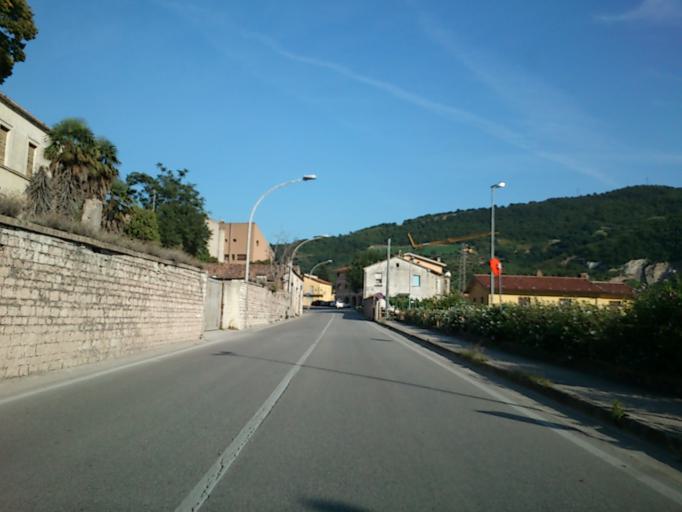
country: IT
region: The Marches
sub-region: Provincia di Pesaro e Urbino
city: Fossombrone
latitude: 43.6881
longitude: 12.8054
